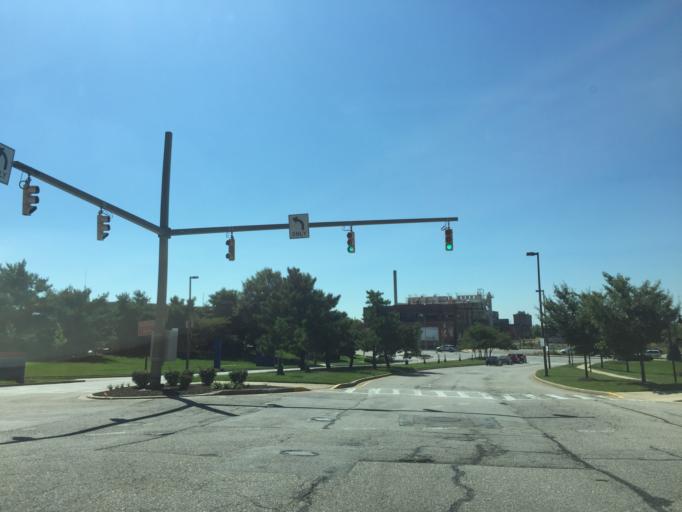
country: US
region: Maryland
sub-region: Baltimore County
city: Rosedale
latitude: 39.2887
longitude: -76.5488
